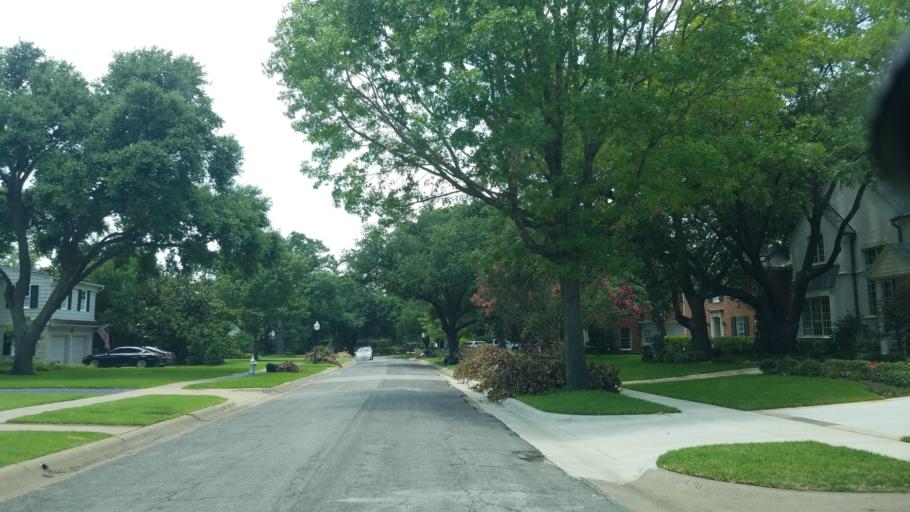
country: US
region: Texas
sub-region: Dallas County
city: University Park
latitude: 32.8443
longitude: -96.8174
